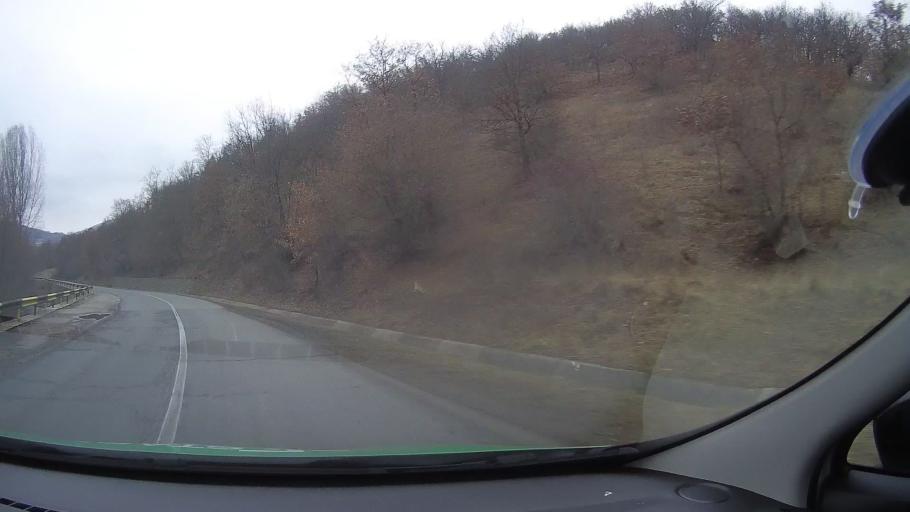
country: RO
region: Alba
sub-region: Comuna Metes
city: Metes
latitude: 46.1042
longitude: 23.4506
